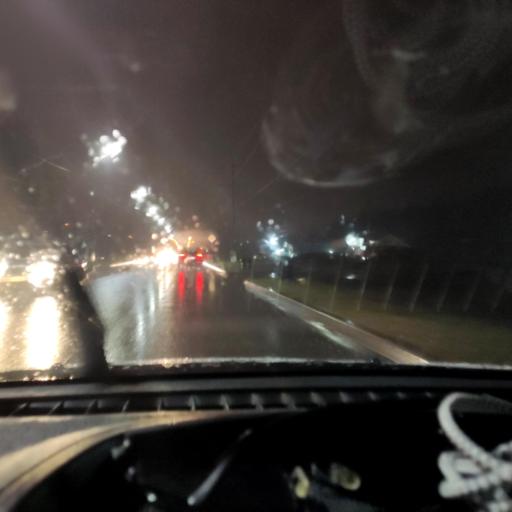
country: RU
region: Samara
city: Tol'yatti
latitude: 53.5170
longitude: 49.3955
